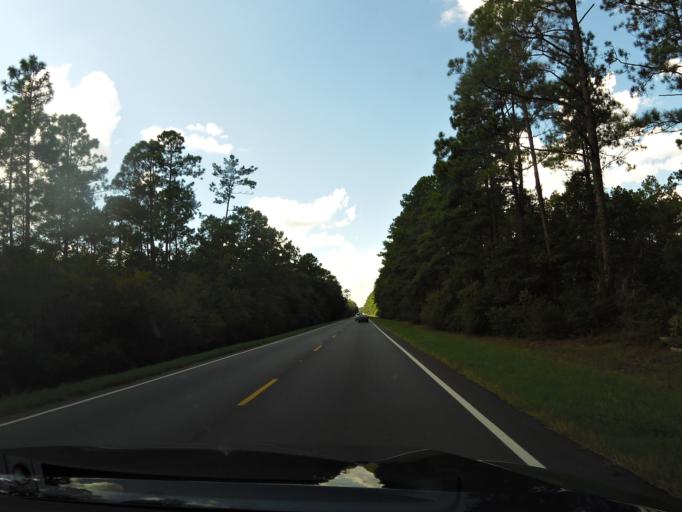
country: US
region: Georgia
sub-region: Echols County
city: Statenville
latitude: 30.7539
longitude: -83.1142
